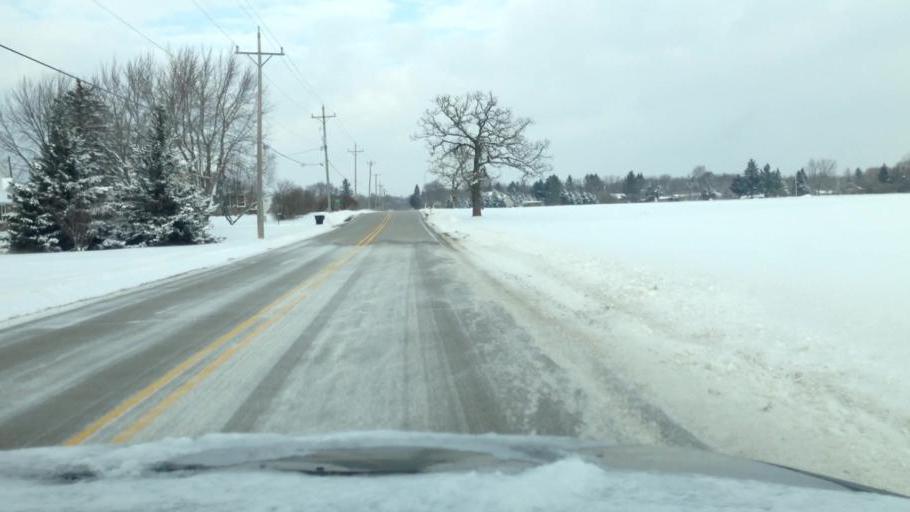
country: US
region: Wisconsin
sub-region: Waukesha County
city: North Prairie
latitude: 42.9016
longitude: -88.4138
